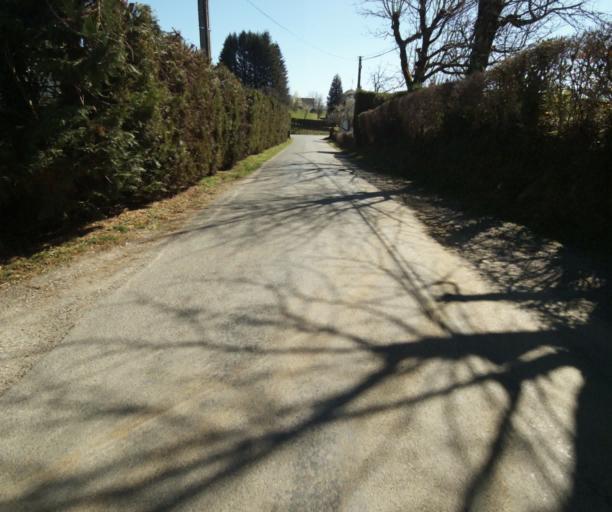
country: FR
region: Limousin
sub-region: Departement de la Correze
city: Seilhac
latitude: 45.3700
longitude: 1.7192
